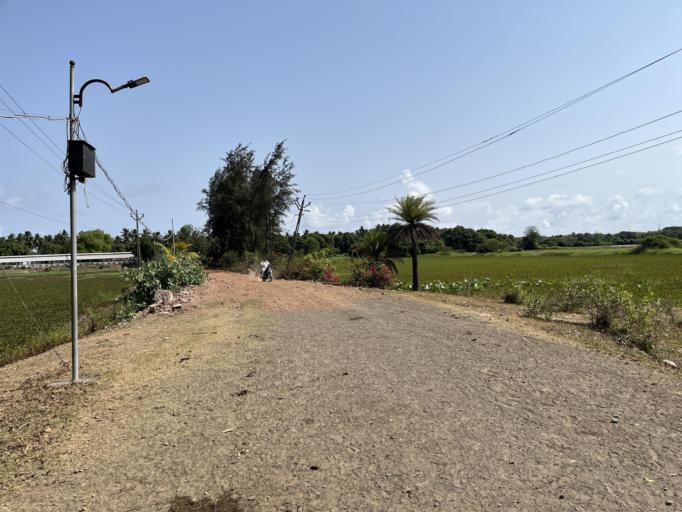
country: IN
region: Daman and Diu
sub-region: Daman District
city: Daman
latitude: 20.3484
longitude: 72.8131
